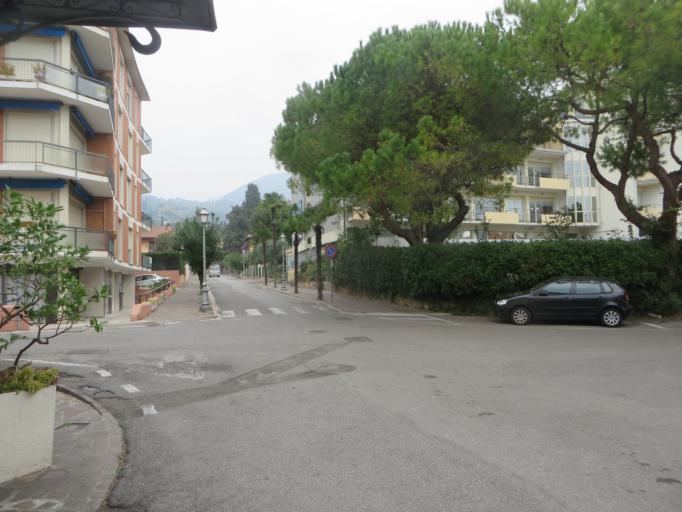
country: IT
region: Lombardy
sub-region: Provincia di Brescia
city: Gardone Riviera
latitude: 45.6133
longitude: 10.5527
